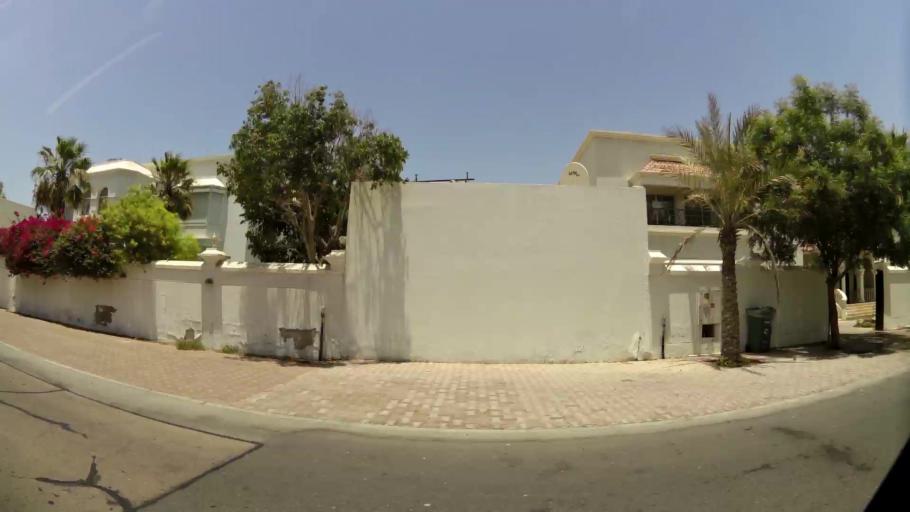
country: AE
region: Dubai
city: Dubai
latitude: 25.2194
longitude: 55.2570
